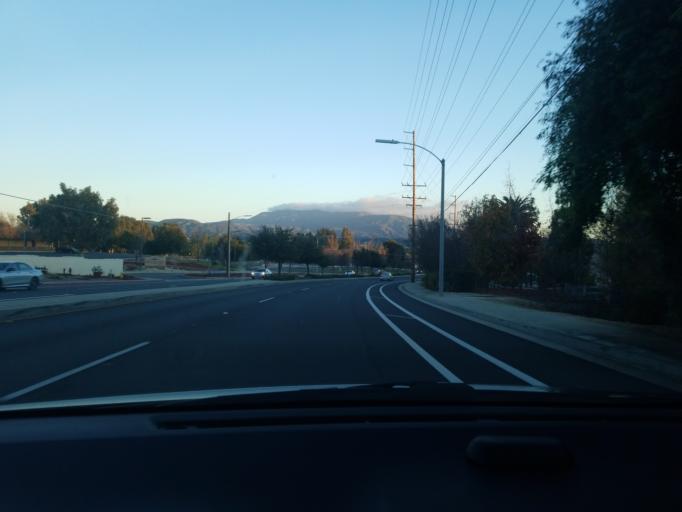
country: US
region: California
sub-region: Riverside County
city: Temecula
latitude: 33.4872
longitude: -117.1049
